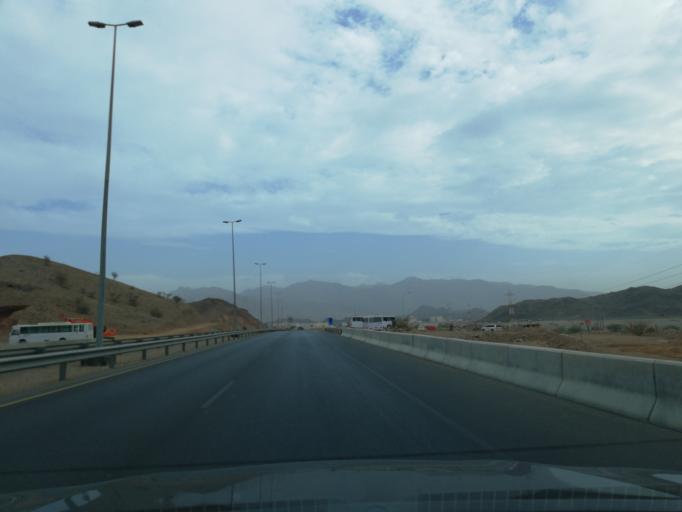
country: OM
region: Muhafazat Masqat
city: Bawshar
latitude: 23.5230
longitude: 58.3481
